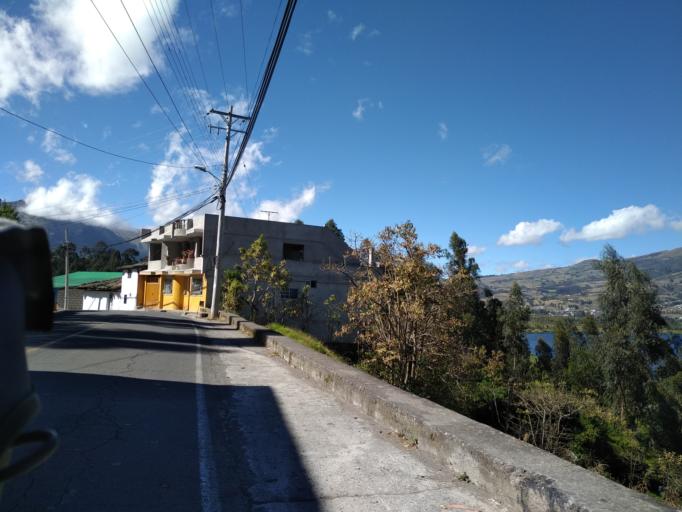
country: EC
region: Imbabura
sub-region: Canton Otavalo
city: Otavalo
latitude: 0.2102
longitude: -78.2082
